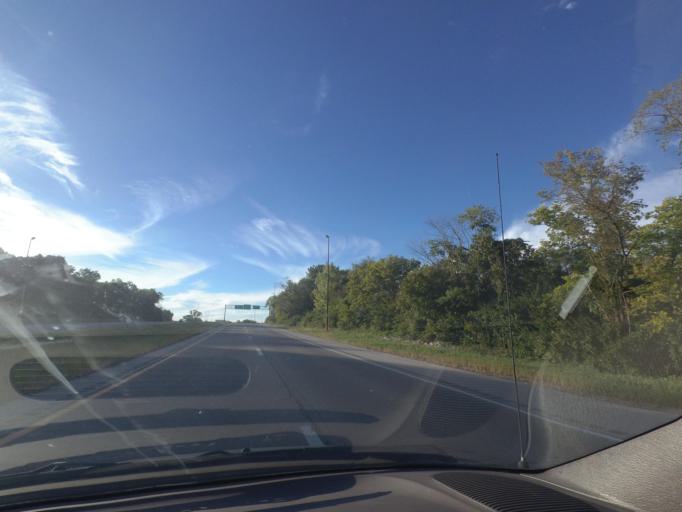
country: US
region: Illinois
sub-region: Sangamon County
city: Grandview
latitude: 39.7835
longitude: -89.5946
